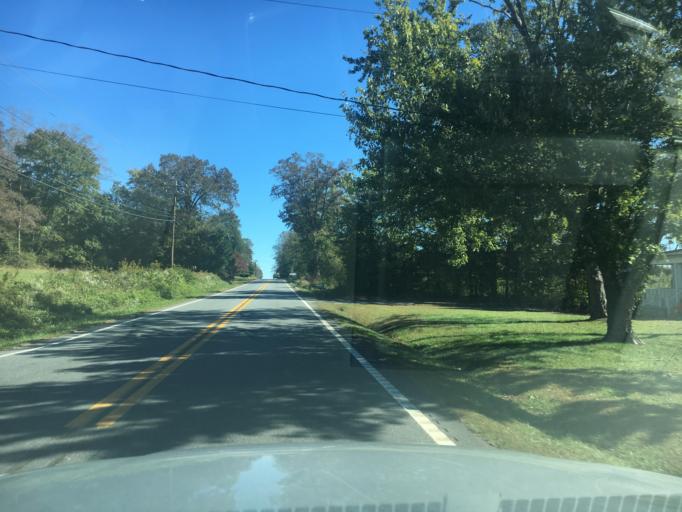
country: US
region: North Carolina
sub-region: Rutherford County
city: Rutherfordton
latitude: 35.3914
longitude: -81.9377
